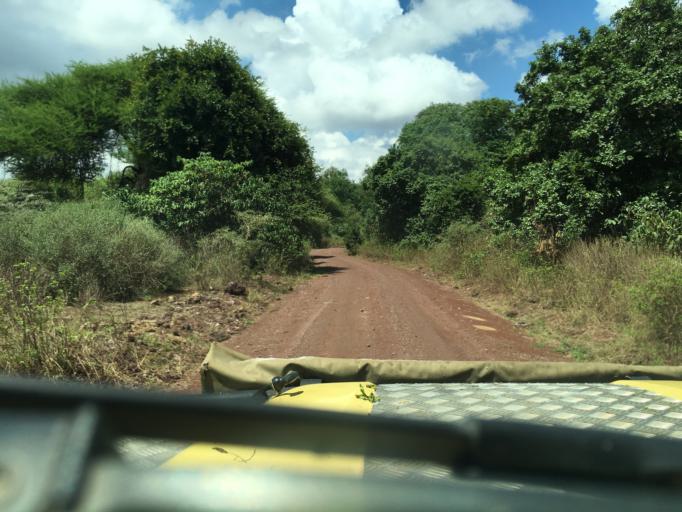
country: TZ
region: Arusha
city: Mto wa Mbu
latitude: -3.4197
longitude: 35.8183
